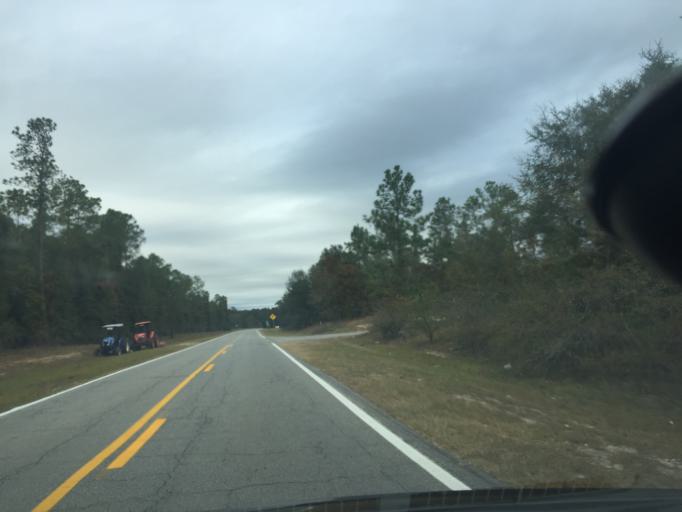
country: US
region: Georgia
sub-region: Chatham County
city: Bloomingdale
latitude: 32.1008
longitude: -81.3817
